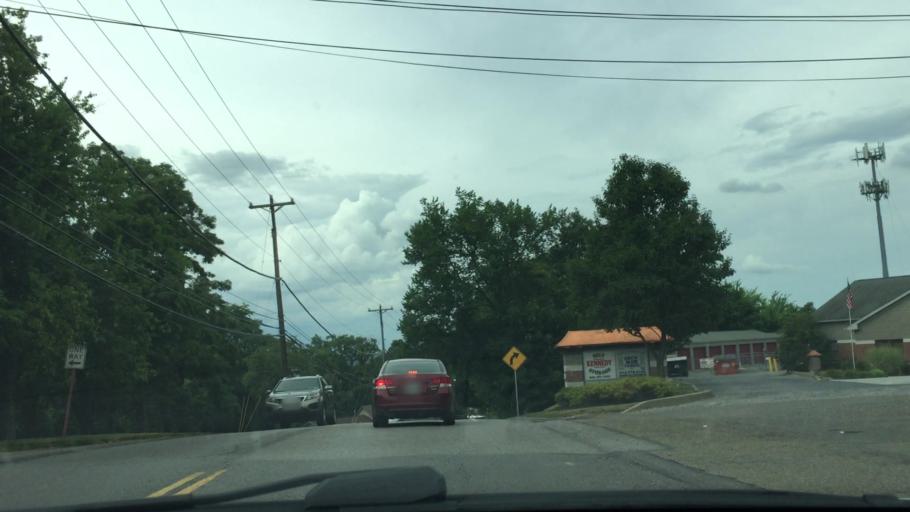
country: US
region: Pennsylvania
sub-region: Allegheny County
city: McKees Rocks
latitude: 40.4729
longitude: -80.1001
